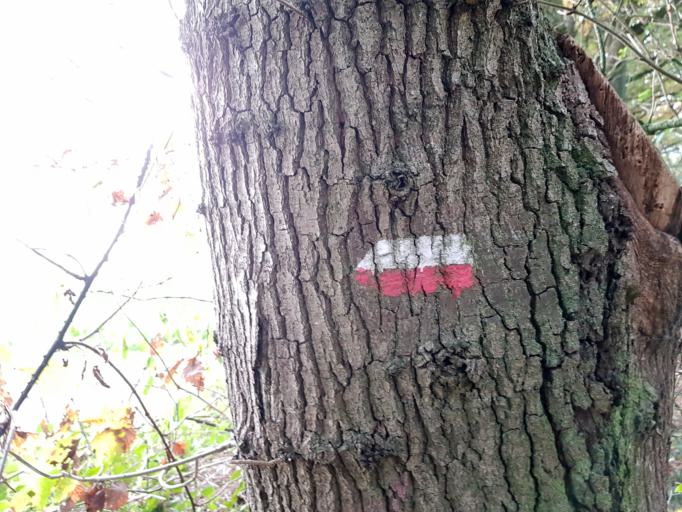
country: NL
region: Gelderland
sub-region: Gemeente Groesbeek
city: Groesbeek
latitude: 51.7612
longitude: 5.9174
